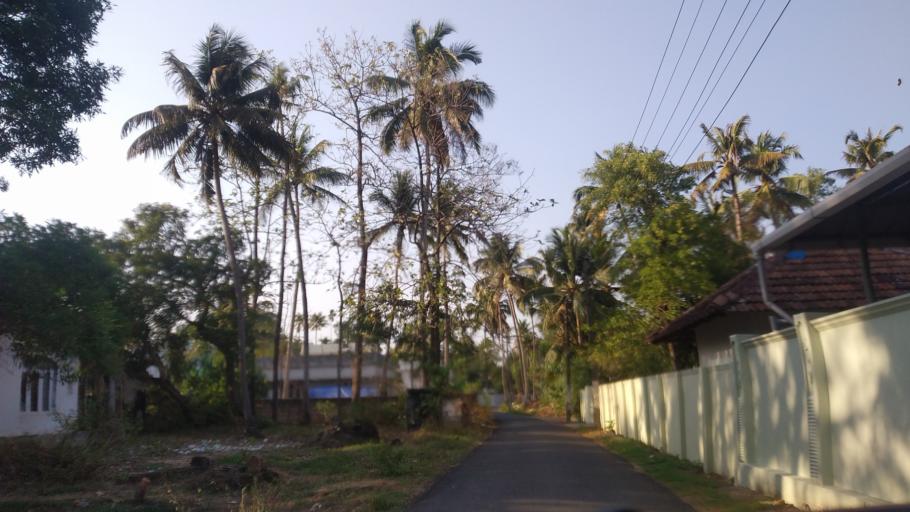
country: IN
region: Kerala
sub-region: Thrissur District
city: Kodungallur
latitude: 10.1347
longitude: 76.2017
